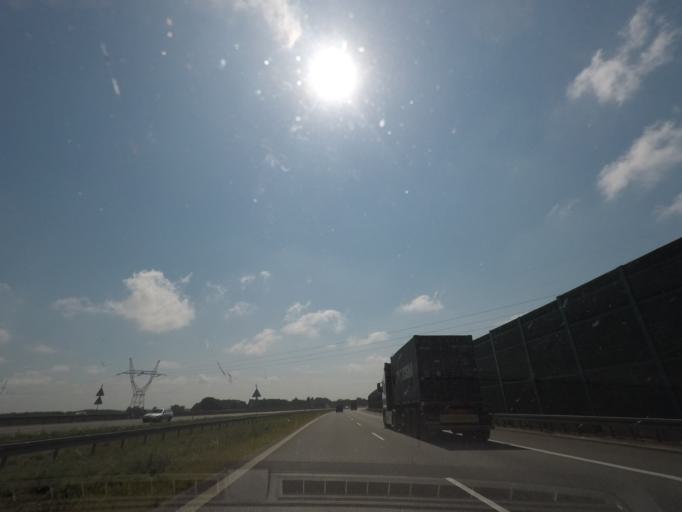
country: PL
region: Kujawsko-Pomorskie
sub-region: Powiat wloclawski
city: Baruchowo
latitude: 52.4361
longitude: 19.2478
